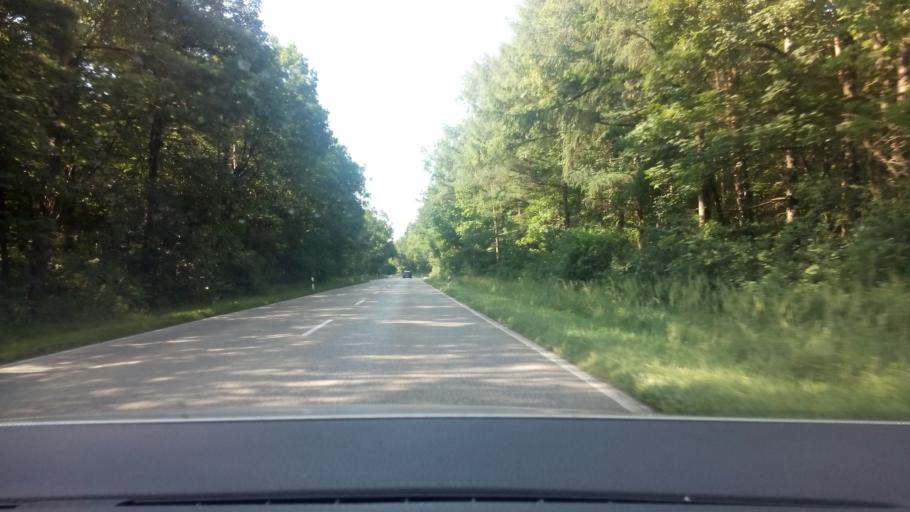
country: DE
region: Bavaria
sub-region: Upper Bavaria
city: Oberschleissheim
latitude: 48.2441
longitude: 11.5828
